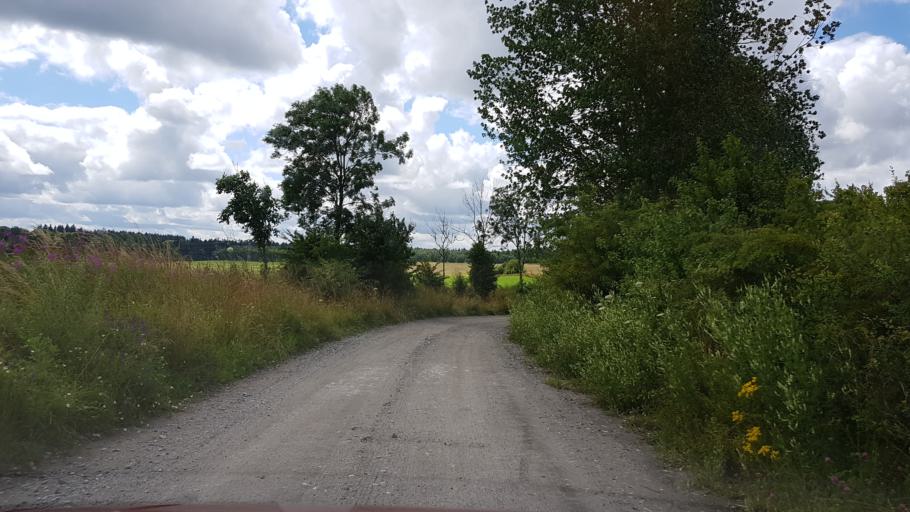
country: PL
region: West Pomeranian Voivodeship
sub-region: Powiat koszalinski
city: Mielno
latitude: 54.1685
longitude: 15.9633
